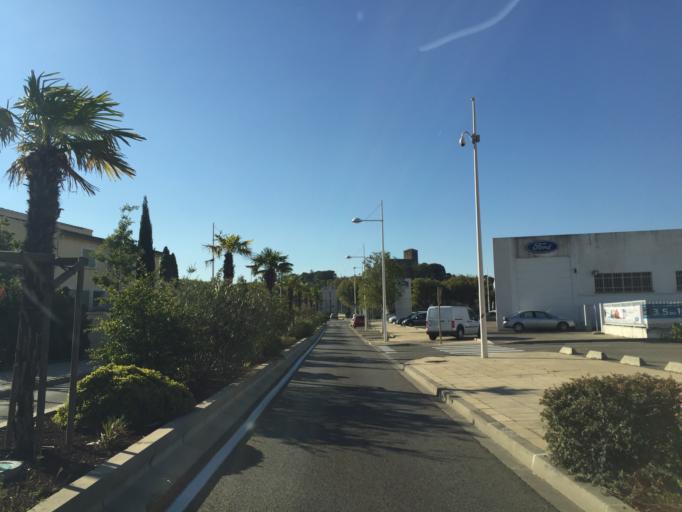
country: FR
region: Provence-Alpes-Cote d'Azur
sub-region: Departement du Vaucluse
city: Bollene
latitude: 44.2837
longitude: 4.7508
